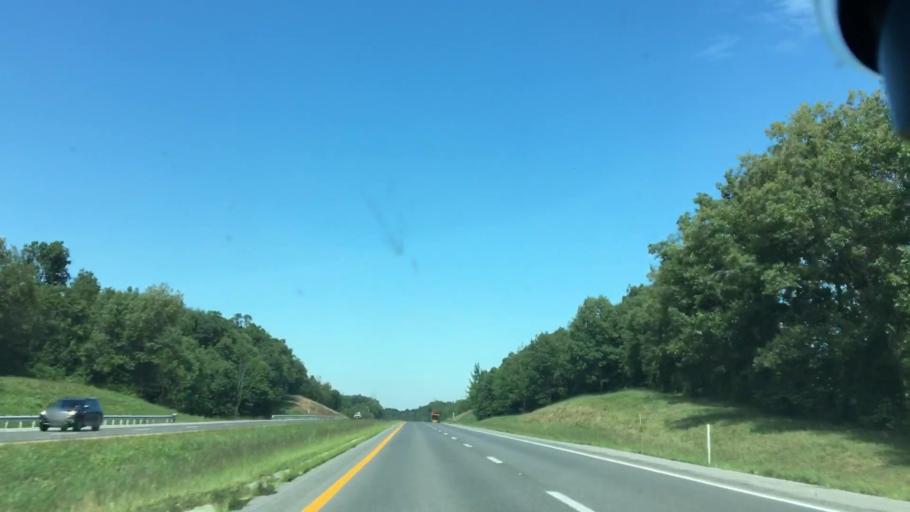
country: US
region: Kentucky
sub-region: Webster County
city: Sebree
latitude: 37.5183
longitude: -87.4748
